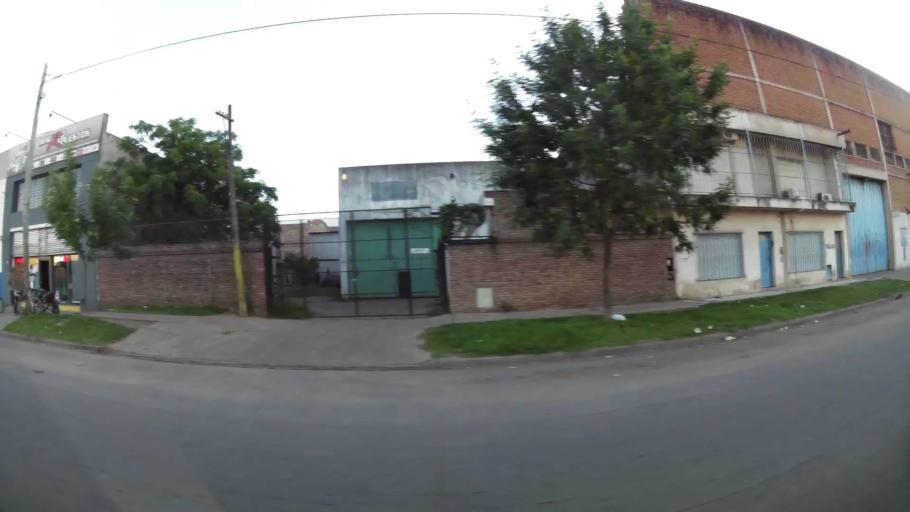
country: AR
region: Santa Fe
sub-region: Departamento de Rosario
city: Rosario
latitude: -32.9720
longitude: -60.6864
